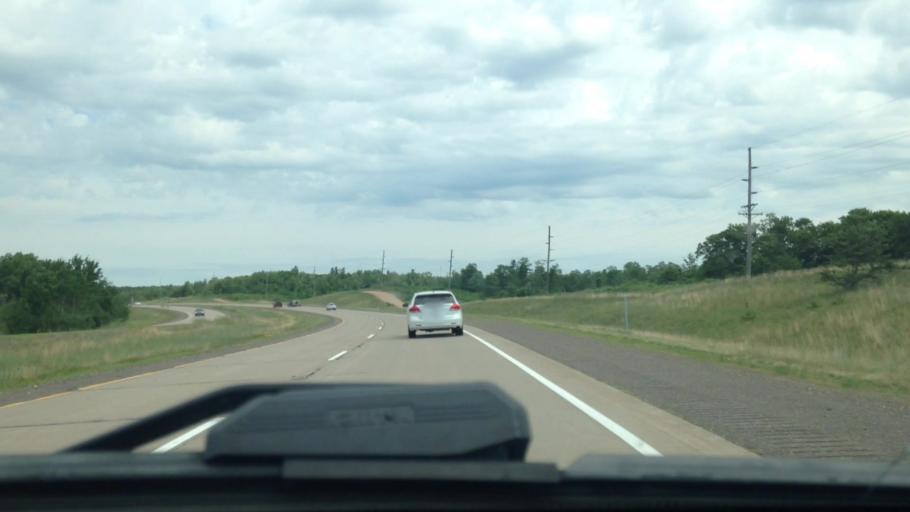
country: US
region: Wisconsin
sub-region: Douglas County
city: Lake Nebagamon
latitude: 46.2100
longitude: -91.7970
